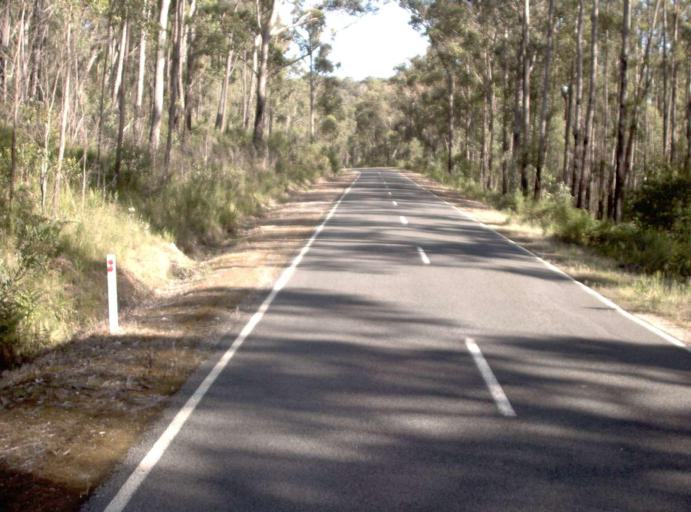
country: AU
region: Victoria
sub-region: East Gippsland
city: Lakes Entrance
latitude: -37.6645
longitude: 148.4779
